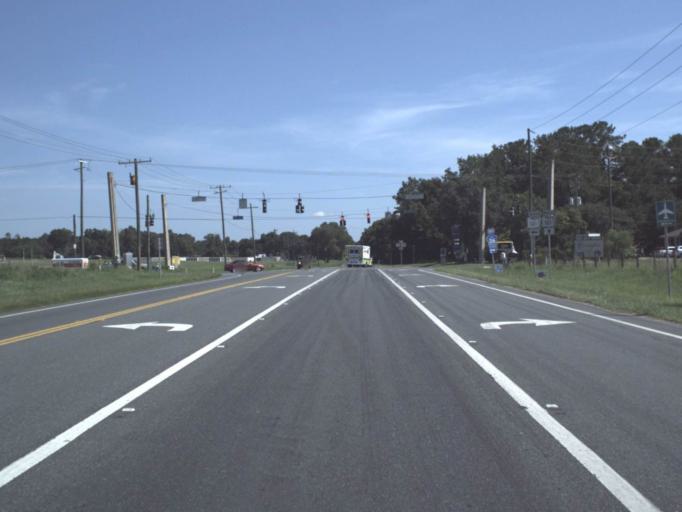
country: US
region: Florida
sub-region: Levy County
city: Williston
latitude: 29.3733
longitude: -82.4558
